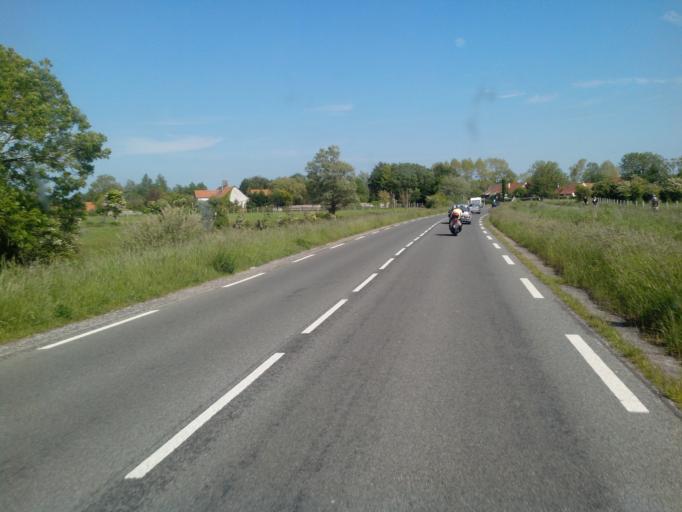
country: FR
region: Nord-Pas-de-Calais
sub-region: Departement du Pas-de-Calais
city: Verton
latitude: 50.3810
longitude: 1.6437
